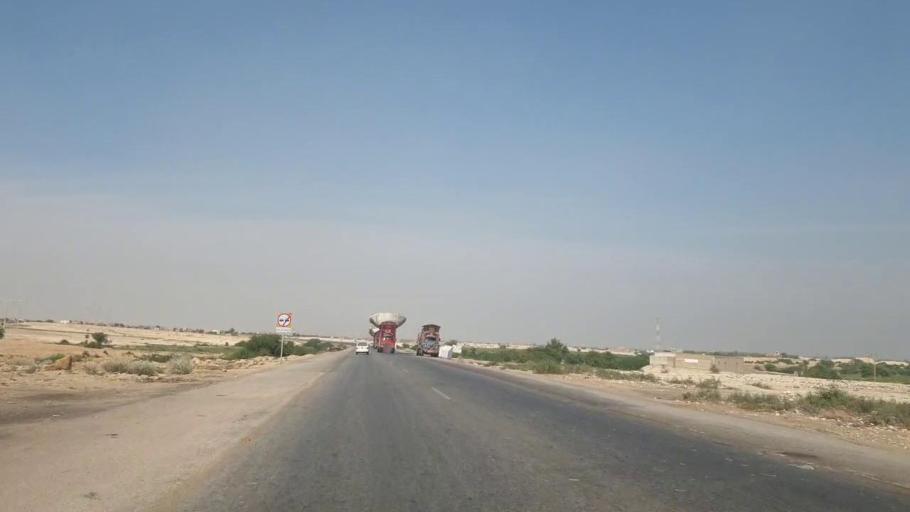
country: PK
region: Sindh
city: Hala
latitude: 25.7944
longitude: 68.2806
